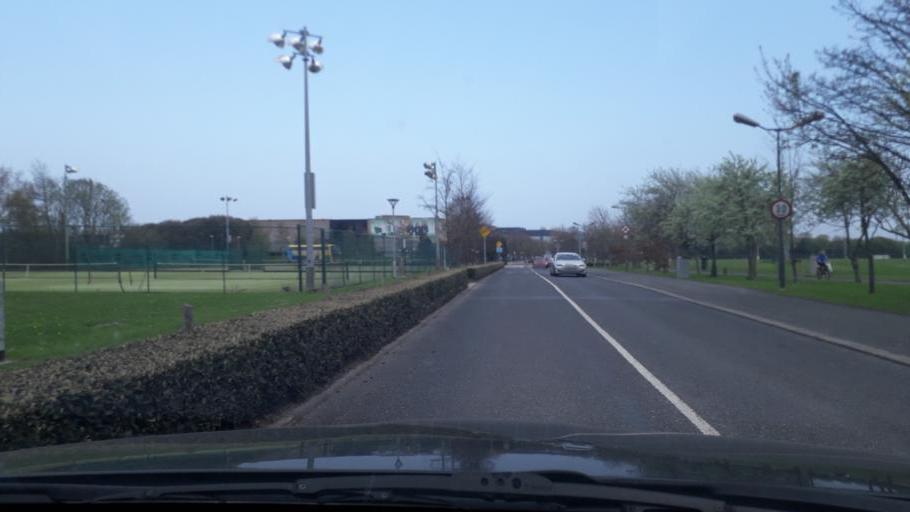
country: IE
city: Clonskeagh
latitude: 53.3079
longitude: -6.2321
